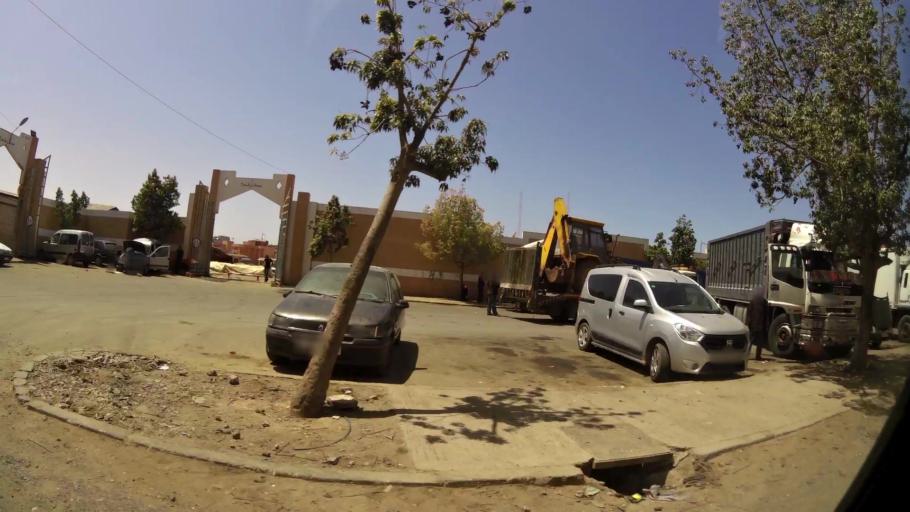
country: MA
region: Souss-Massa-Draa
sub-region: Inezgane-Ait Mellou
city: Inezgane
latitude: 30.3273
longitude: -9.4953
